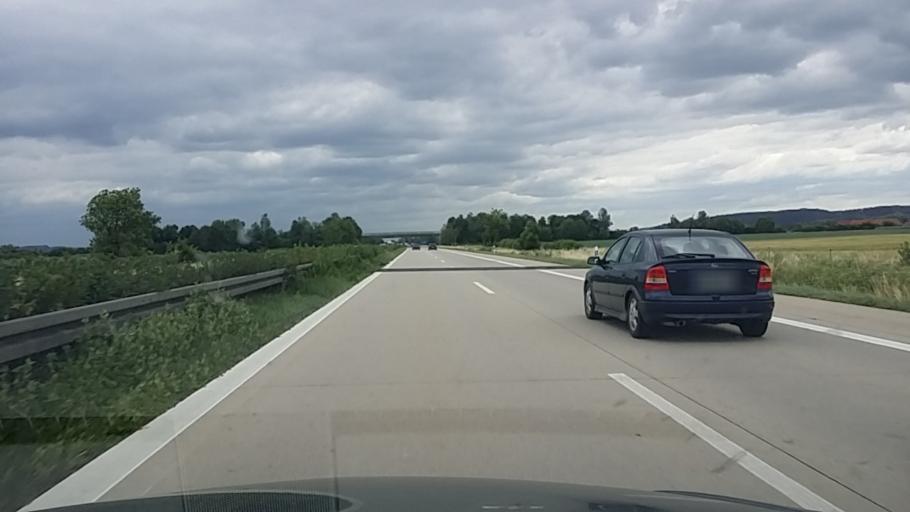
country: DE
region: Bavaria
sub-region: Lower Bavaria
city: Essenbach
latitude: 48.6123
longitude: 12.2675
